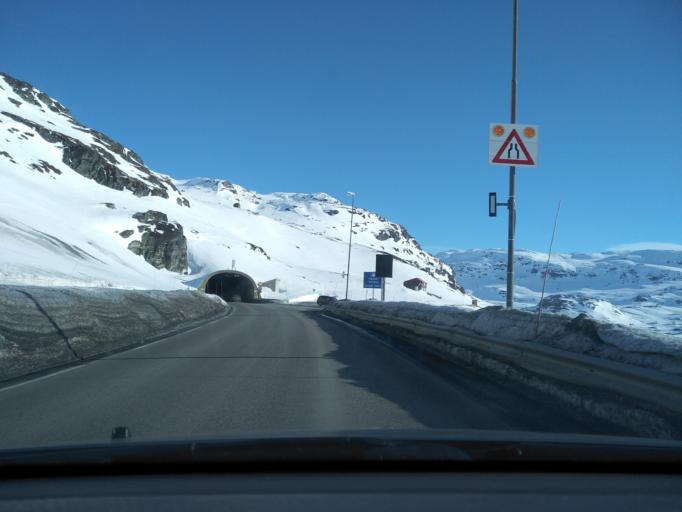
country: NO
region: Aust-Agder
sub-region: Bykle
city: Hovden
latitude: 59.8394
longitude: 6.9872
